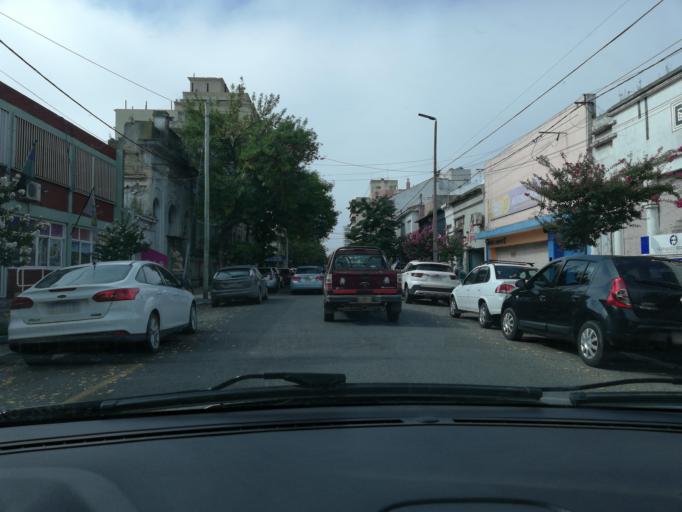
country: AR
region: Buenos Aires
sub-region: Partido de Balcarce
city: Balcarce
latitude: -37.8484
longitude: -58.2552
